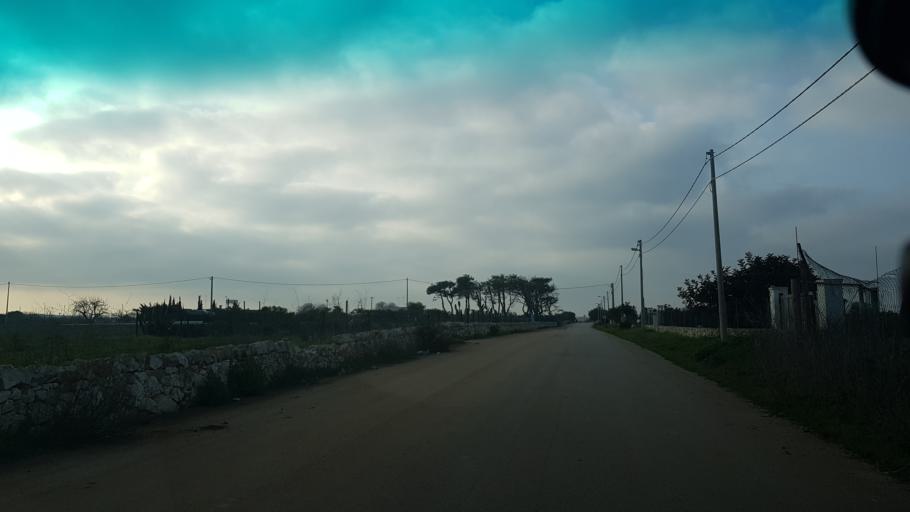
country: IT
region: Apulia
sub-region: Provincia di Brindisi
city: Carovigno
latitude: 40.7430
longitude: 17.7281
